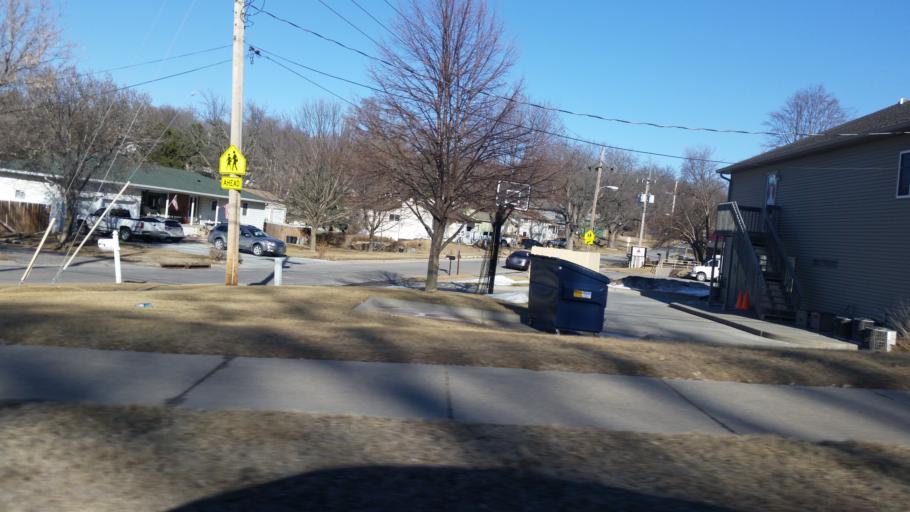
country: US
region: Nebraska
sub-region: Sarpy County
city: Bellevue
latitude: 41.1632
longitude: -95.9224
